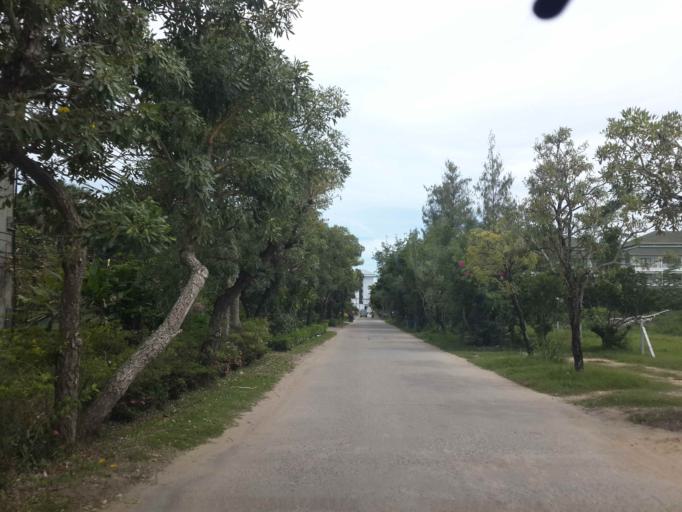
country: TH
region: Prachuap Khiri Khan
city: Hua Hin
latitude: 12.5341
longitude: 99.9677
